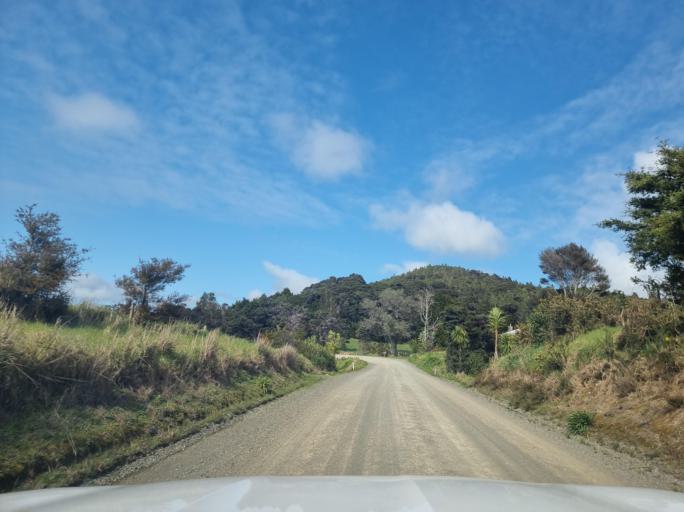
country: NZ
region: Auckland
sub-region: Auckland
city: Wellsford
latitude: -36.1011
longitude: 174.4979
